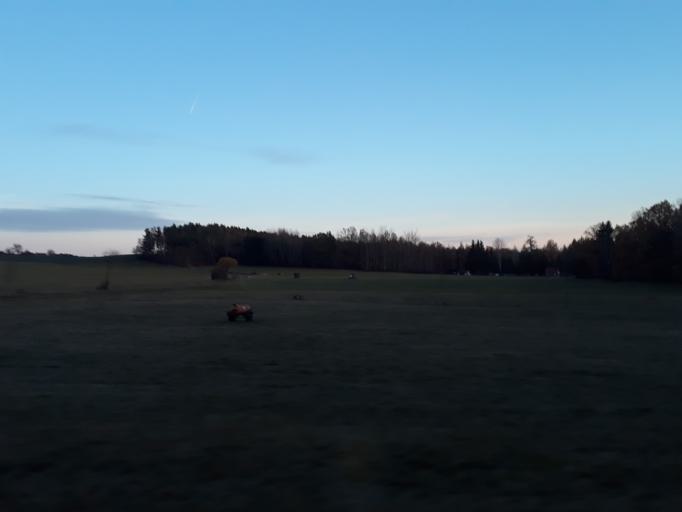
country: DE
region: Saxony
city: Reinhardtsgrimma
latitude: 50.8998
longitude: 13.7824
